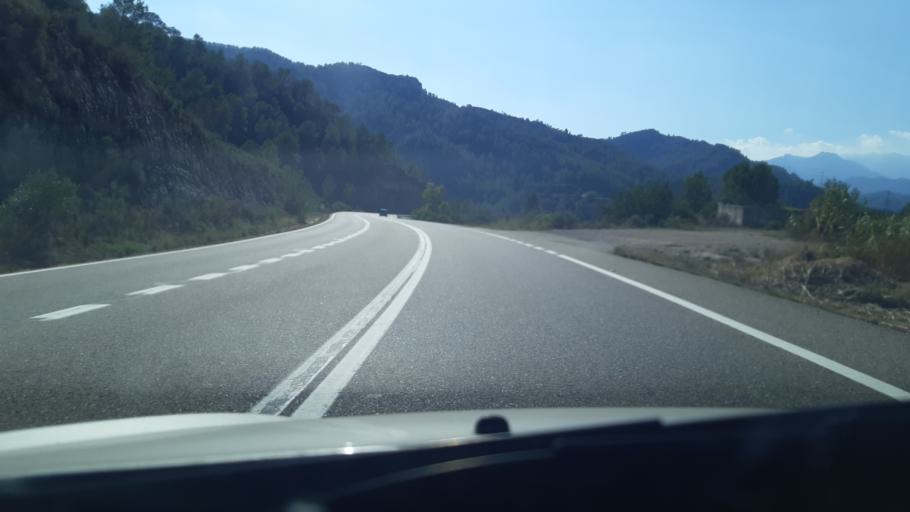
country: ES
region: Catalonia
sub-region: Provincia de Tarragona
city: Benifallet
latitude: 40.9870
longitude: 0.5383
